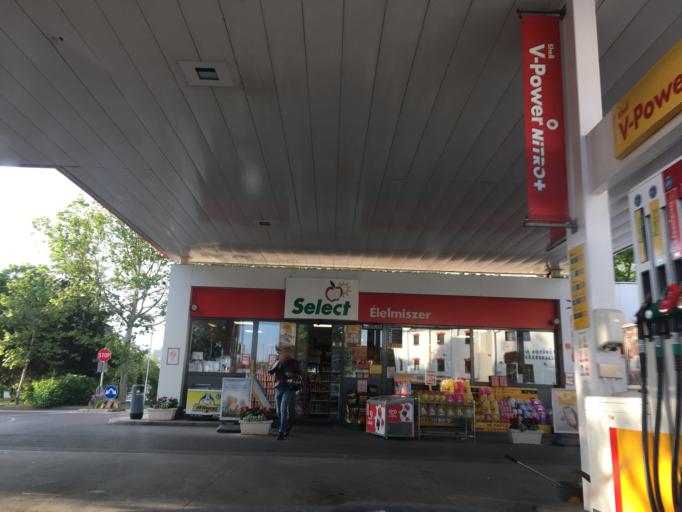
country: HU
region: Hajdu-Bihar
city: Debrecen
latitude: 47.5352
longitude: 21.6124
